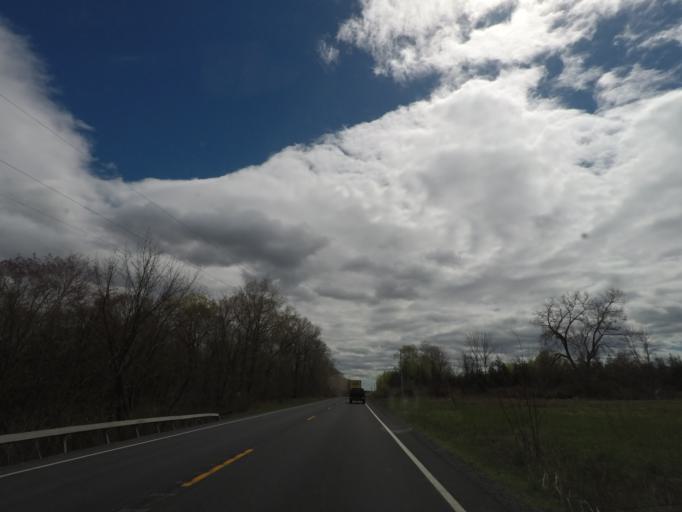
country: US
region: New York
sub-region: Albany County
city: Ravena
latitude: 42.4963
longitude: -73.7948
